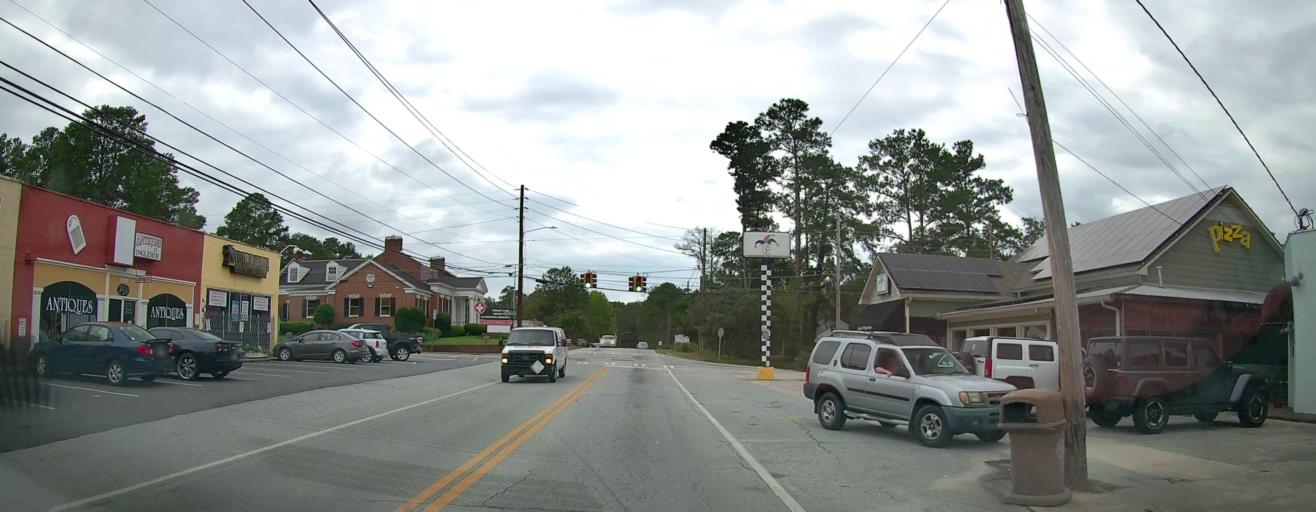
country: US
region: Georgia
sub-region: Bibb County
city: Macon
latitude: 32.8538
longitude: -83.6569
